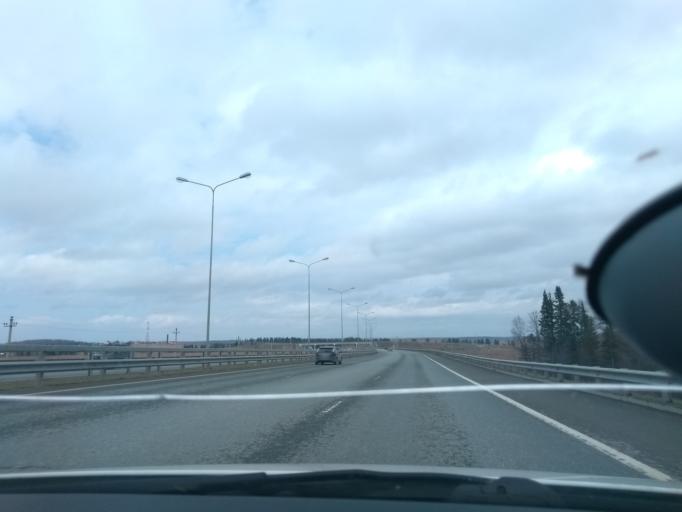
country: RU
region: Perm
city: Zvezdnyy
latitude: 57.7764
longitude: 56.3386
